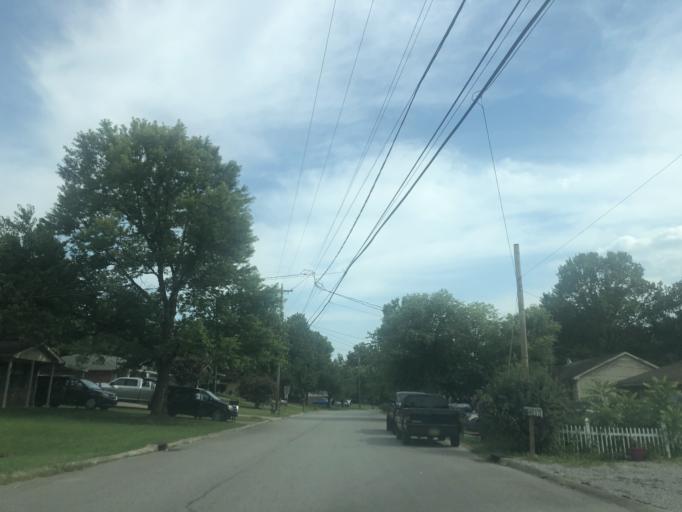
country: US
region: Tennessee
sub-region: Wilson County
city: Green Hill
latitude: 36.1740
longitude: -86.5914
